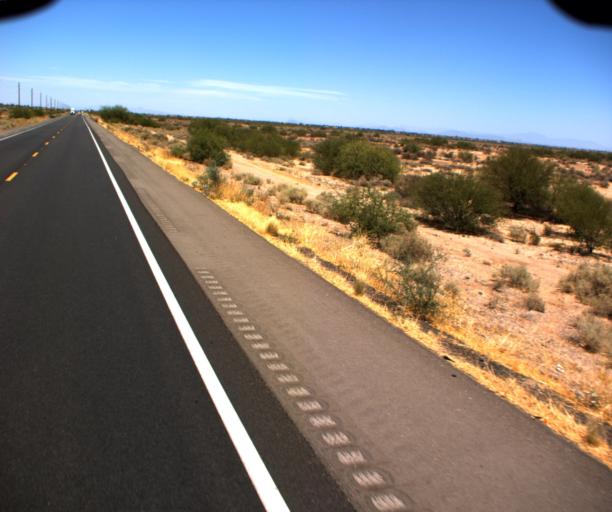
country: US
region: Arizona
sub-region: Maricopa County
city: Sun Lakes
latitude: 33.1773
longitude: -111.8409
